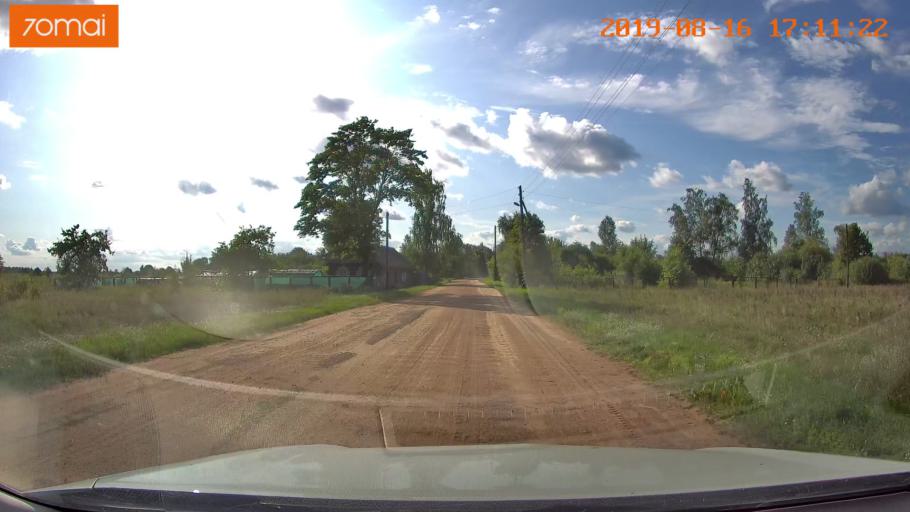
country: BY
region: Mogilev
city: Hlusha
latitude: 53.1955
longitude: 28.9071
